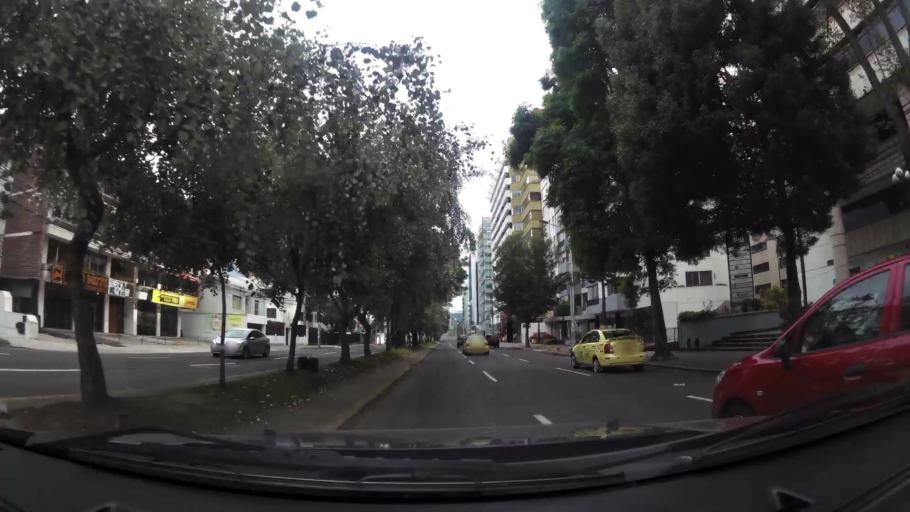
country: EC
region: Pichincha
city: Quito
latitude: -0.1947
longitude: -78.4846
